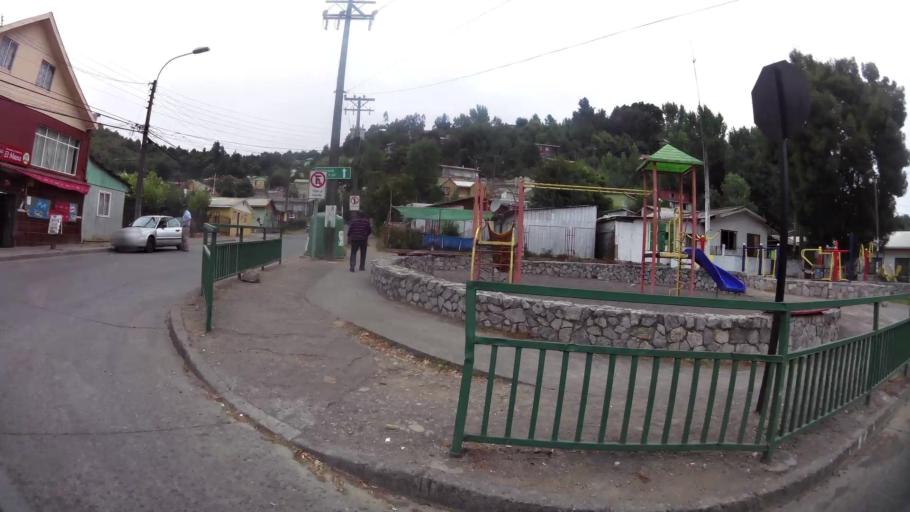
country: CL
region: Biobio
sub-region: Provincia de Concepcion
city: Concepcion
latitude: -36.8360
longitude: -73.0008
